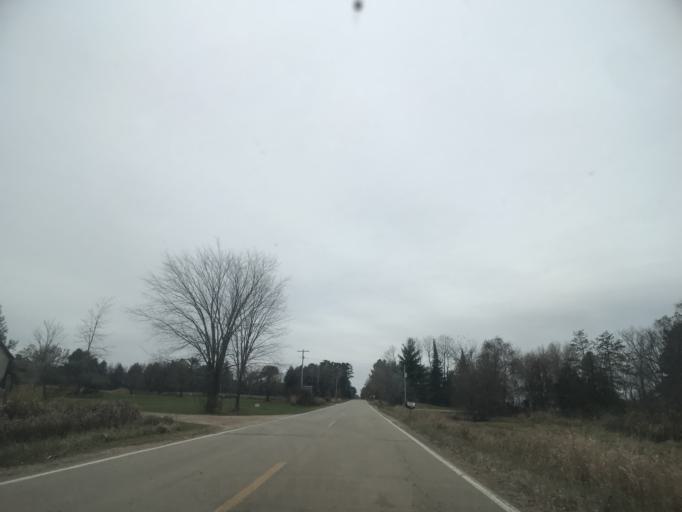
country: US
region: Wisconsin
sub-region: Oconto County
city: Gillett
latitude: 44.9837
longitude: -88.3195
